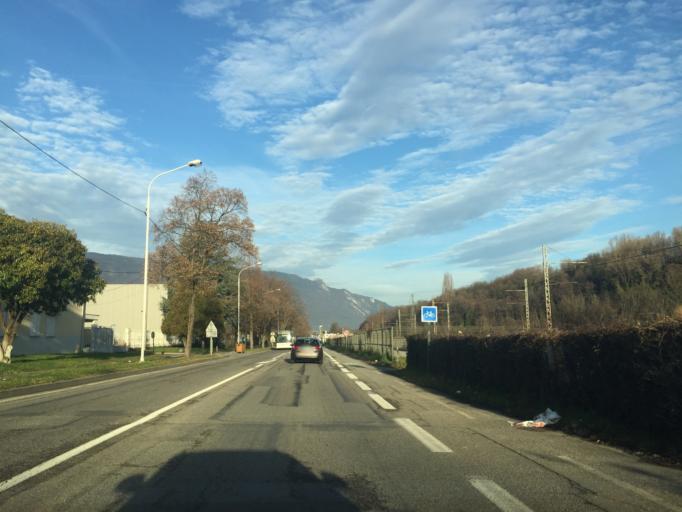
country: FR
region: Rhone-Alpes
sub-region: Departement de la Savoie
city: Cognin
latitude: 45.5883
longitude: 5.9060
